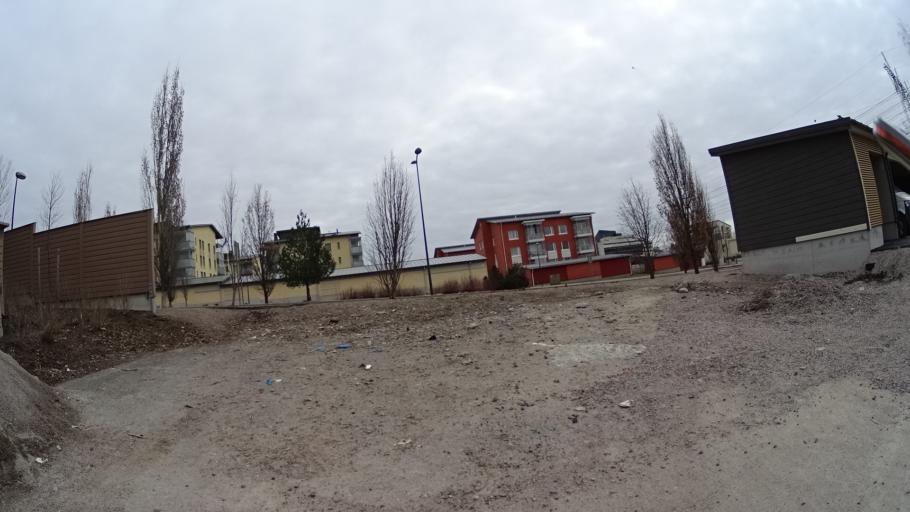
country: FI
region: Uusimaa
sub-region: Helsinki
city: Vantaa
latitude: 60.2904
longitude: 24.9438
